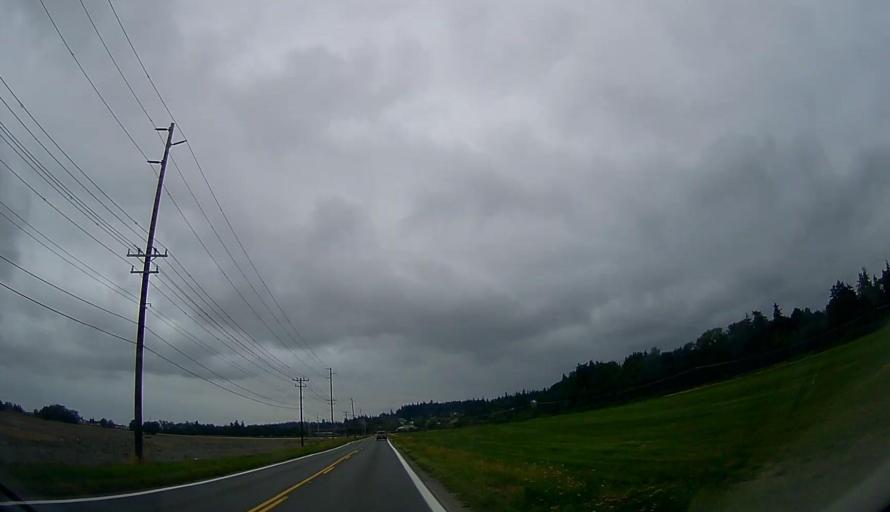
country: US
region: Washington
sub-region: Snohomish County
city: Stanwood
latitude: 48.2324
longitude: -122.3466
